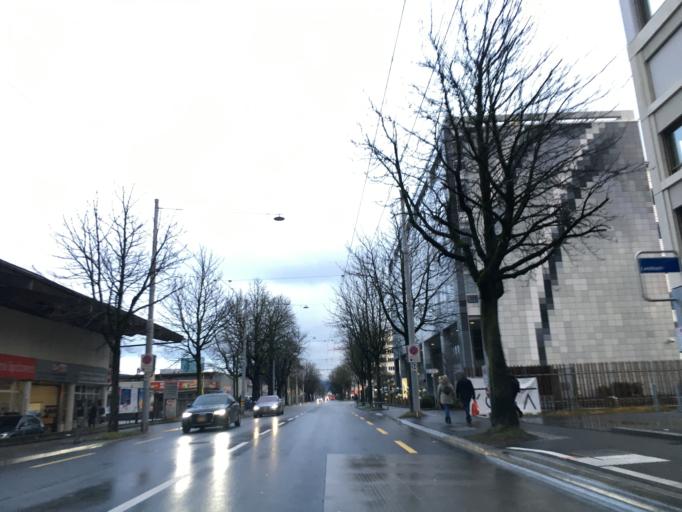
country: CH
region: Zurich
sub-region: Bezirk Zuerich
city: Zuerich (Kreis 9) / Altstetten
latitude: 47.3889
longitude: 8.4953
